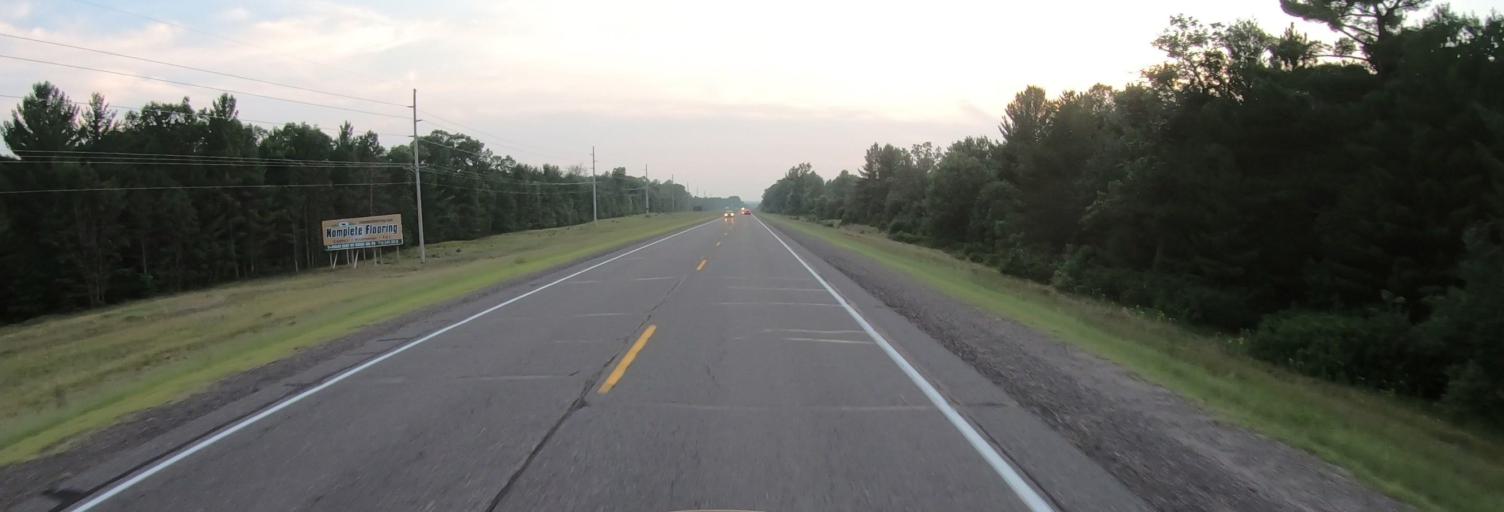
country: US
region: Wisconsin
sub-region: Burnett County
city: Grantsburg
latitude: 45.7731
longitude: -92.7461
